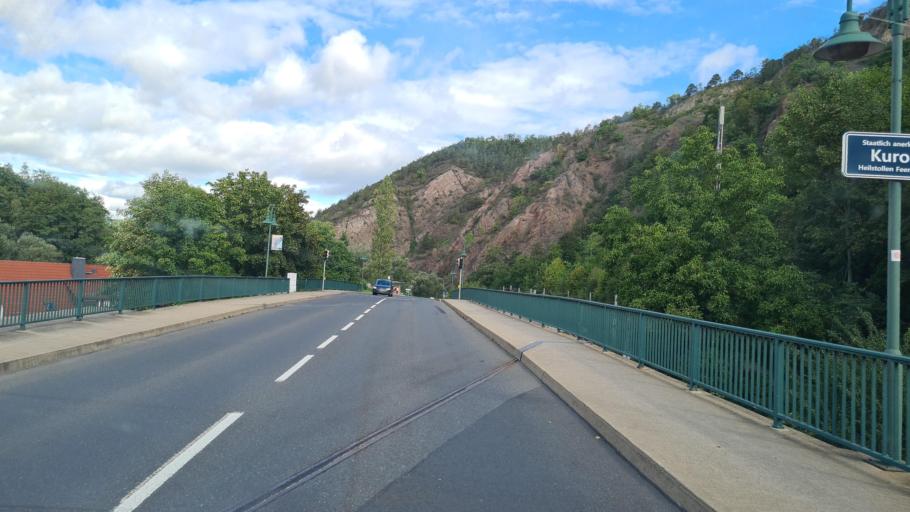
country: DE
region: Thuringia
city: Saalfeld
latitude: 50.6288
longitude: 11.3817
